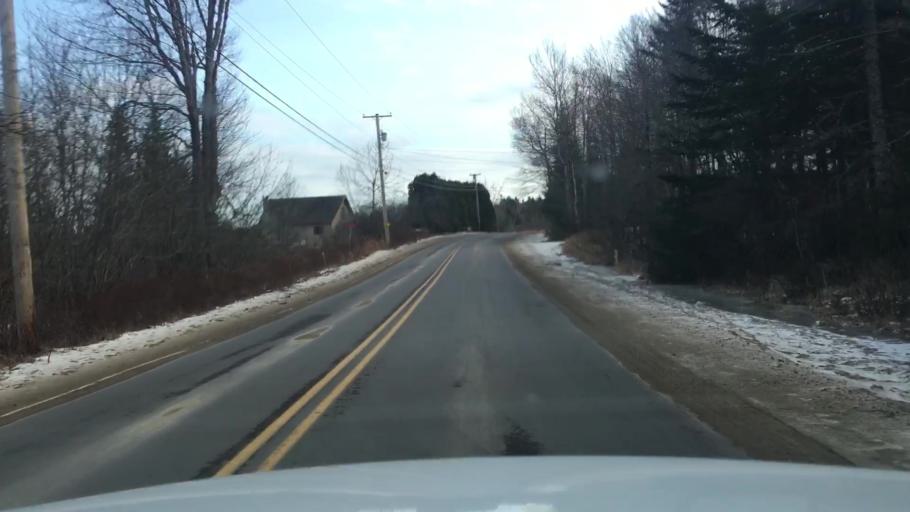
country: US
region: Maine
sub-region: Washington County
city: Jonesport
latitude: 44.6143
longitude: -67.6034
